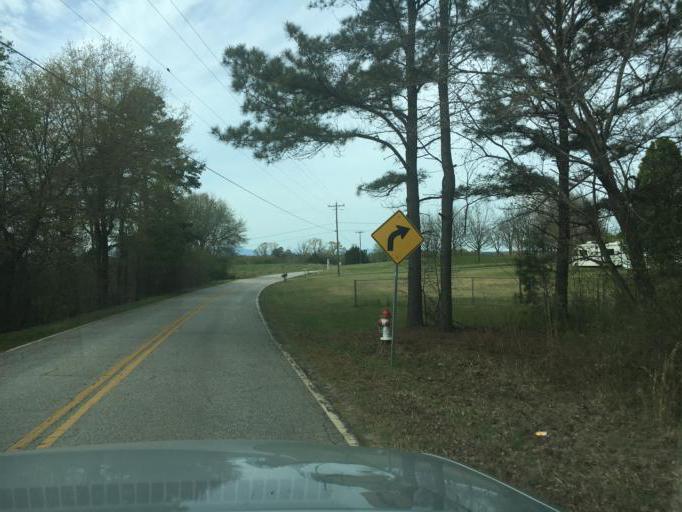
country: US
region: South Carolina
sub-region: Spartanburg County
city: Duncan
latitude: 34.9182
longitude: -82.1651
